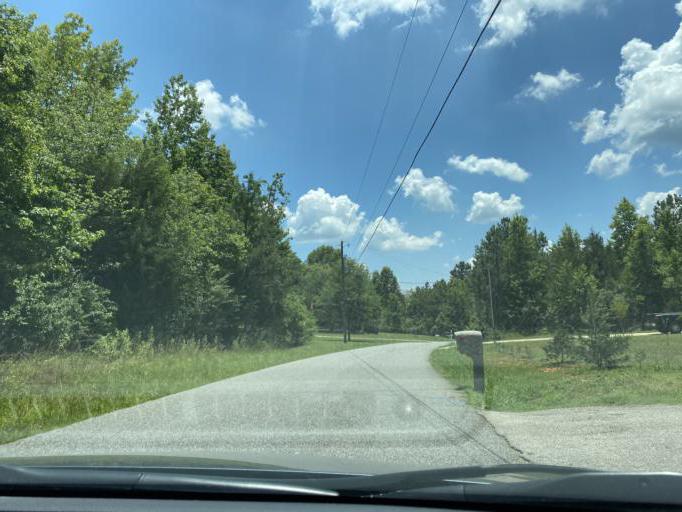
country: US
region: South Carolina
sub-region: Cherokee County
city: Gaffney
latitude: 35.1292
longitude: -81.7188
